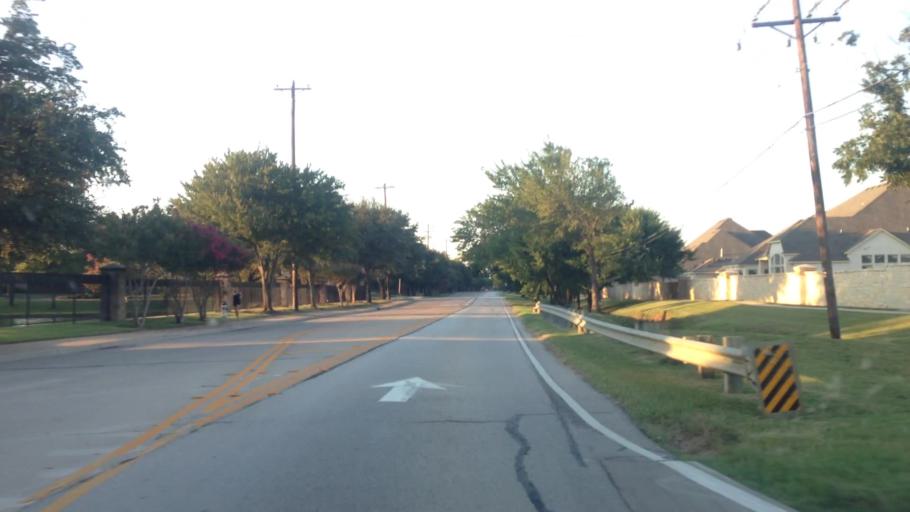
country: US
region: Texas
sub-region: Tarrant County
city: Southlake
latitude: 32.9378
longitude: -97.1336
